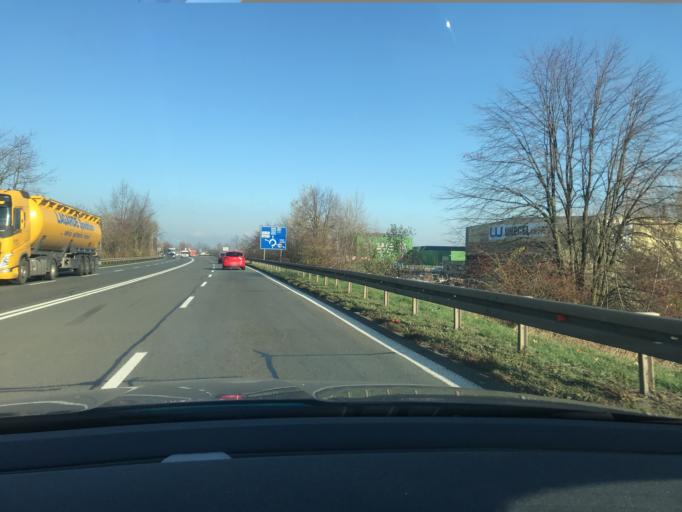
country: CZ
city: Stezery
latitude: 50.2179
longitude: 15.7880
